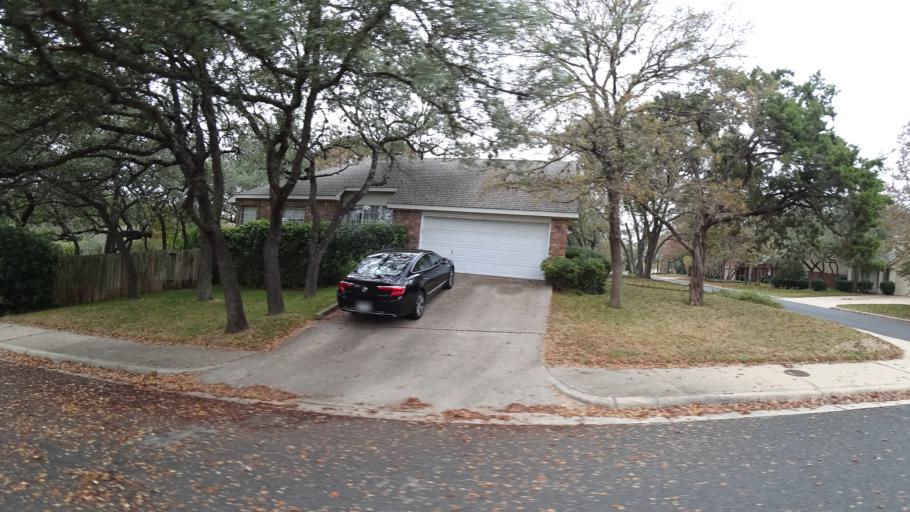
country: US
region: Texas
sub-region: Williamson County
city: Jollyville
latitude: 30.3845
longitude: -97.8003
